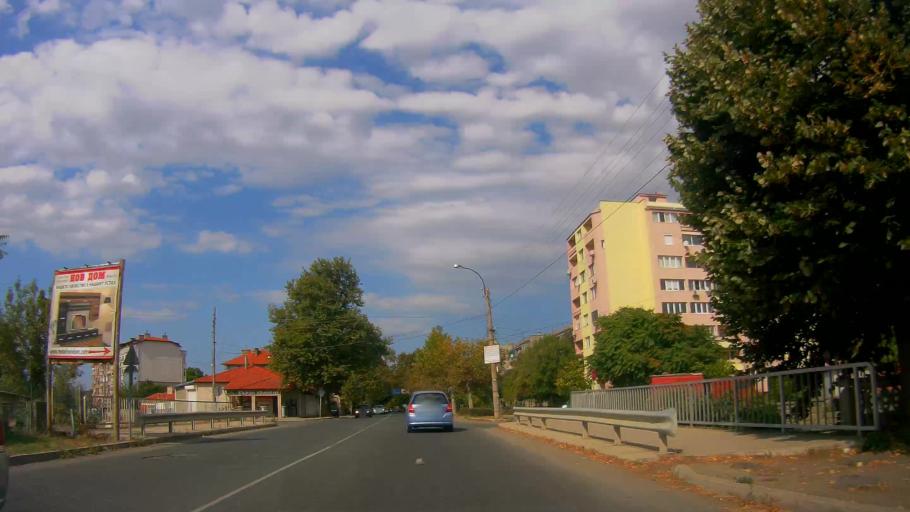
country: BG
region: Burgas
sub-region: Obshtina Aytos
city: Aytos
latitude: 42.6980
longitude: 27.2550
